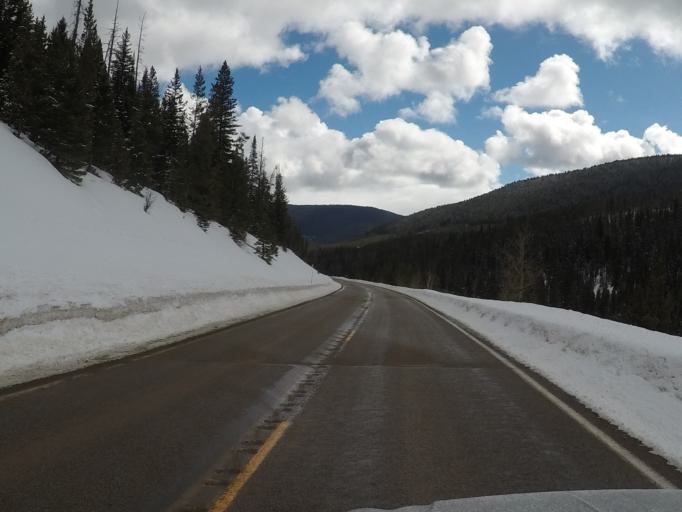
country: US
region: Montana
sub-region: Meagher County
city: White Sulphur Springs
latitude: 46.8078
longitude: -110.7064
